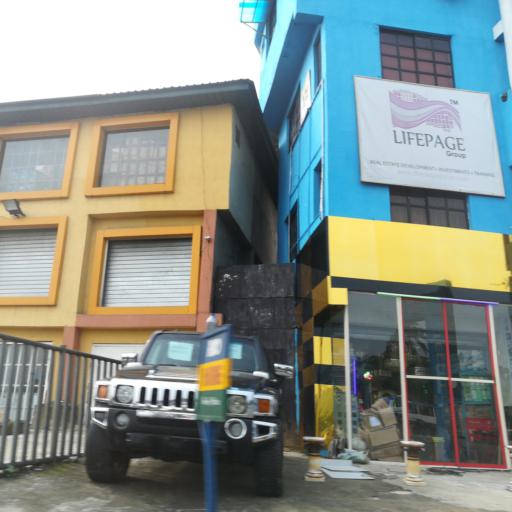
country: NG
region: Rivers
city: Port Harcourt
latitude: 4.8498
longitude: 7.0531
